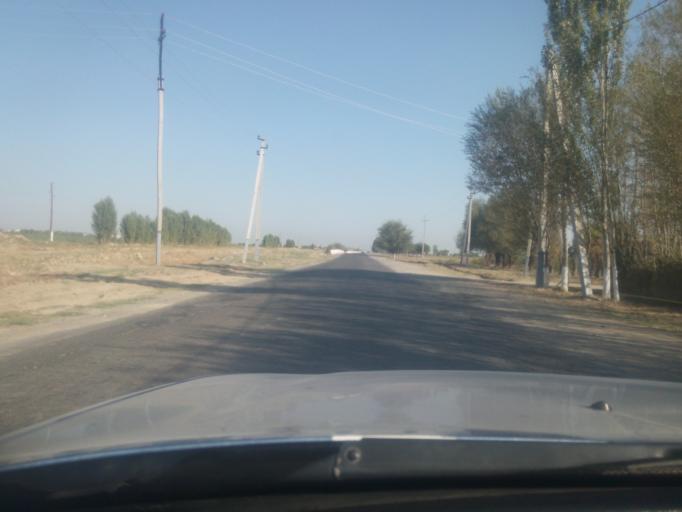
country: UZ
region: Sirdaryo
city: Guliston
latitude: 40.4972
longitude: 68.7995
